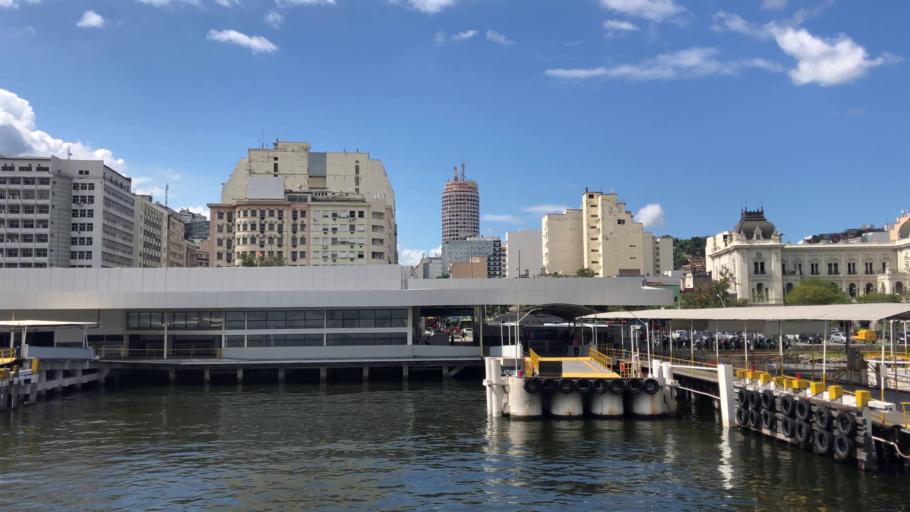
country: BR
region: Rio de Janeiro
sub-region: Niteroi
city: Niteroi
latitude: -22.8900
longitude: -43.1256
